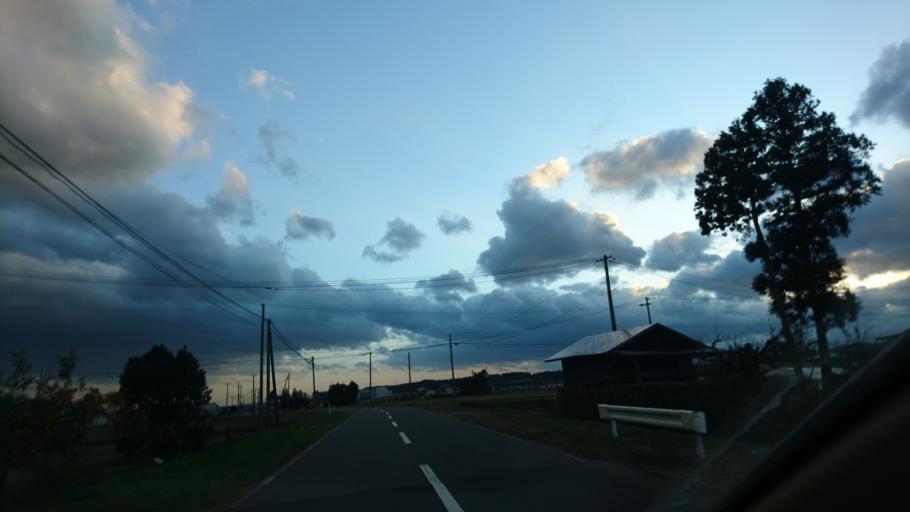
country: JP
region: Iwate
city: Mizusawa
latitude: 39.1042
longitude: 141.1480
